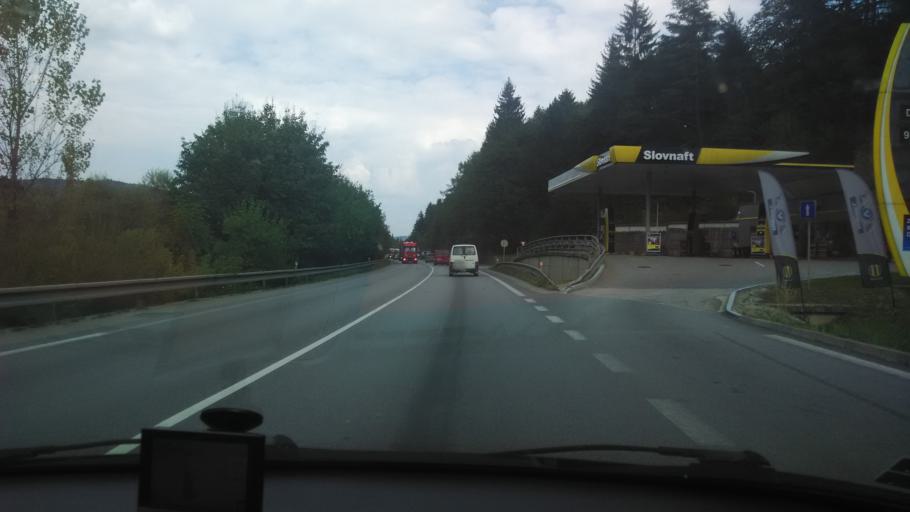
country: SK
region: Zilinsky
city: Kysucke Nove Mesto
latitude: 49.2890
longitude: 18.7808
